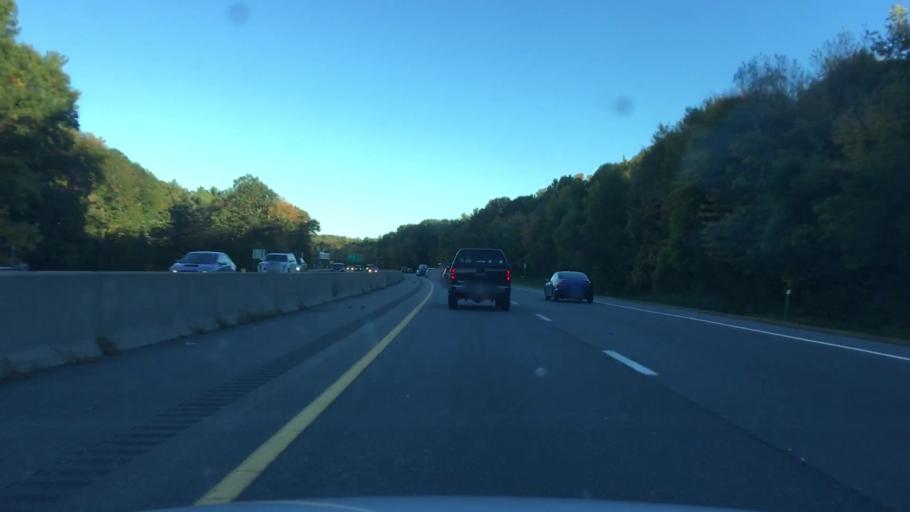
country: US
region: New Hampshire
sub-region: Rockingham County
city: Hampton Falls
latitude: 42.9675
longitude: -70.8866
